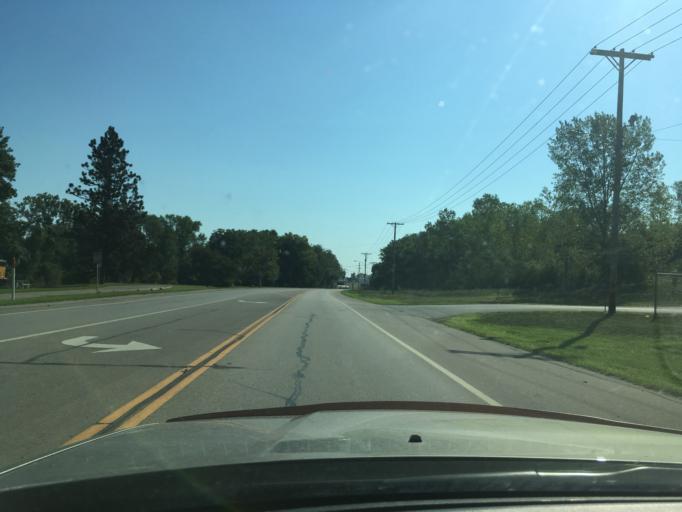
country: US
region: Kansas
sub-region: Atchison County
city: Atchison
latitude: 39.5563
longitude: -95.1466
